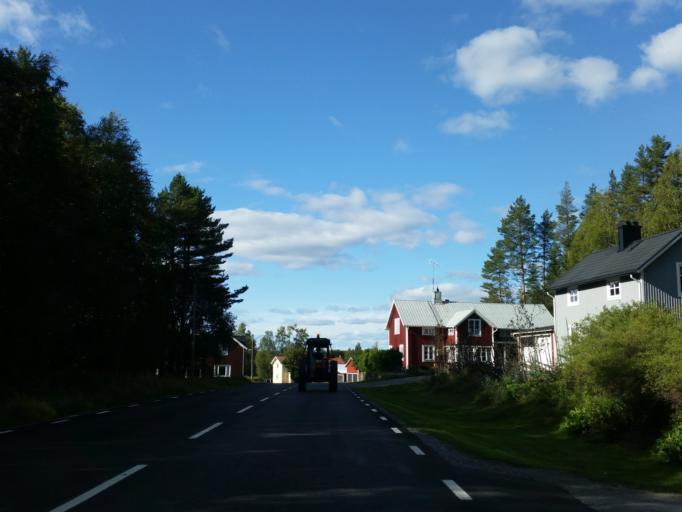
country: SE
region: Vaesterbotten
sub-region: Robertsfors Kommun
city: Robertsfors
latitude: 64.1645
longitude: 20.9325
